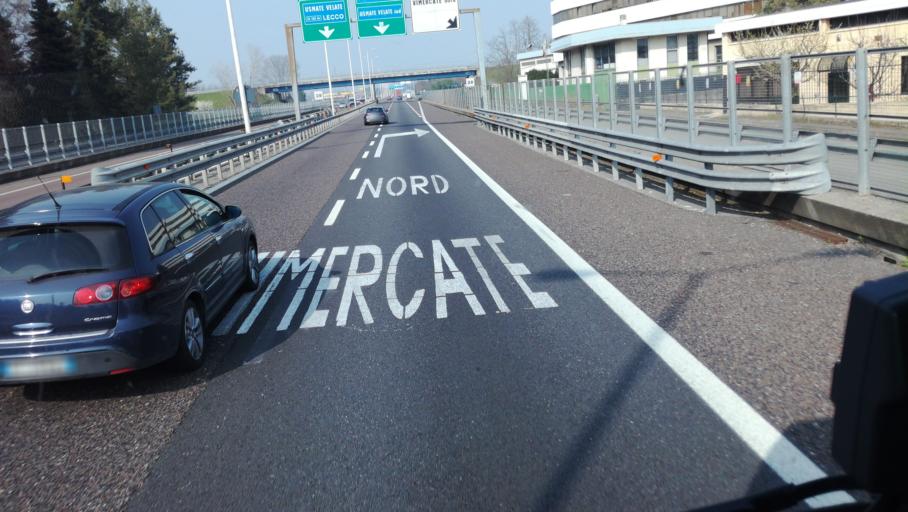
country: IT
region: Lombardy
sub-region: Provincia di Monza e Brianza
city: Velasca
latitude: 45.6310
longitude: 9.3627
